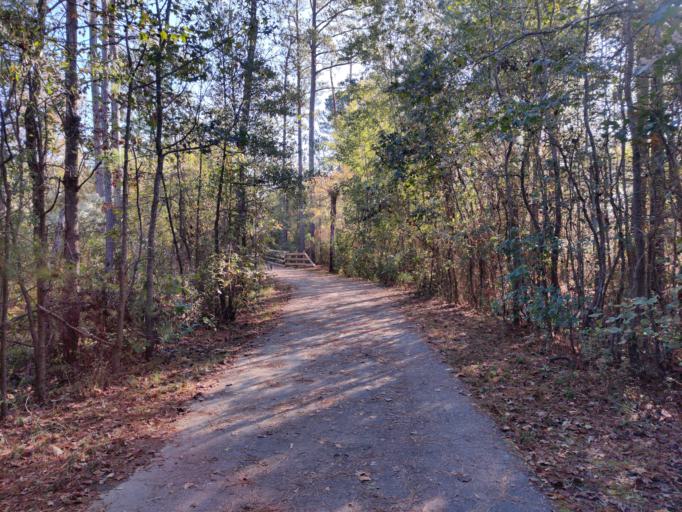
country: US
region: North Carolina
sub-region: Wake County
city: Morrisville
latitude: 35.8167
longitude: -78.8332
